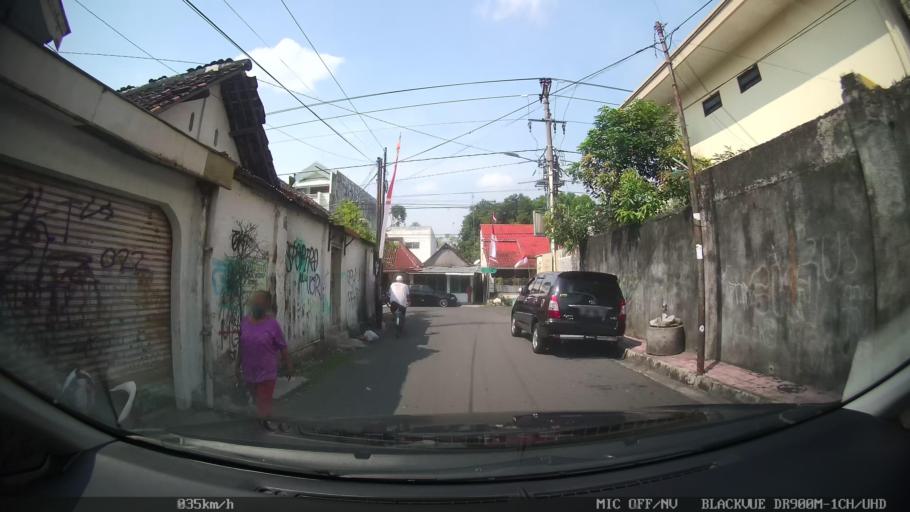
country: ID
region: Daerah Istimewa Yogyakarta
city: Yogyakarta
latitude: -7.7931
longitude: 110.3603
